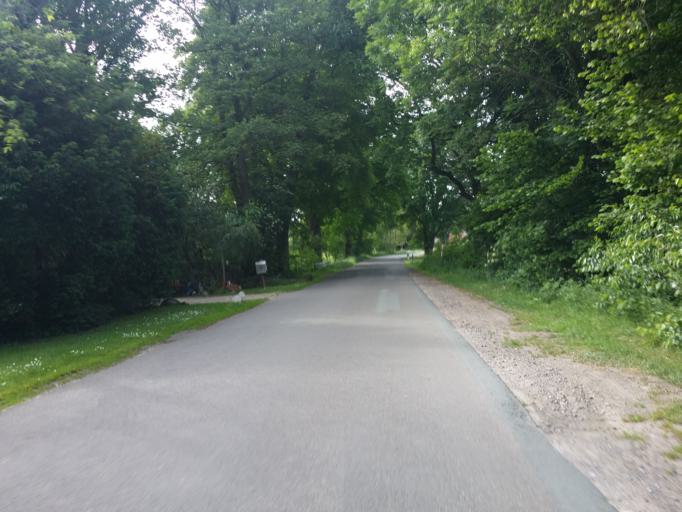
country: DE
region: Lower Saxony
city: Bockhorn
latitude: 53.3655
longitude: 8.0071
